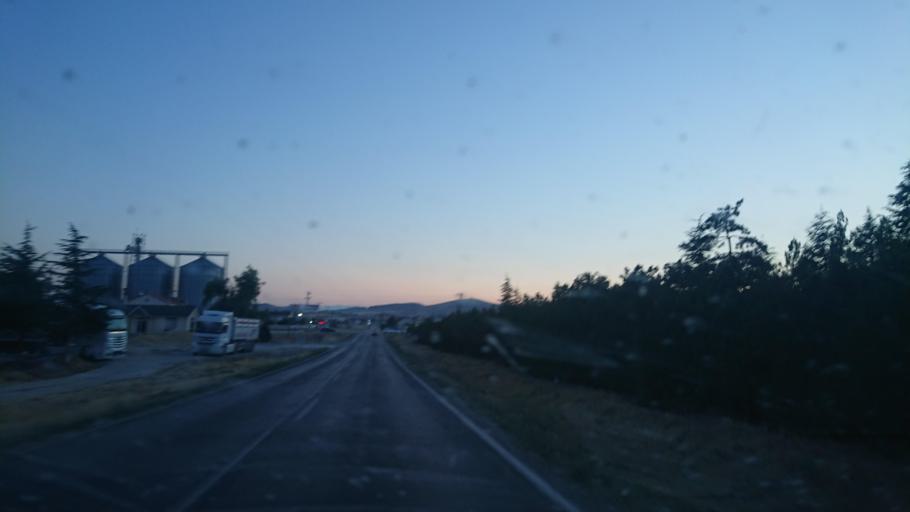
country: TR
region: Aksaray
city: Balci
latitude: 38.7628
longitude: 34.0888
